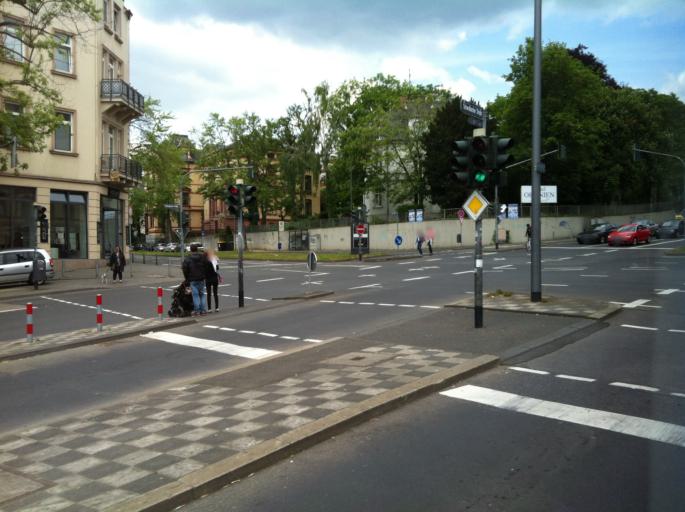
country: DE
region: Hesse
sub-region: Regierungsbezirk Darmstadt
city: Wiesbaden
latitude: 50.0830
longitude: 8.2359
